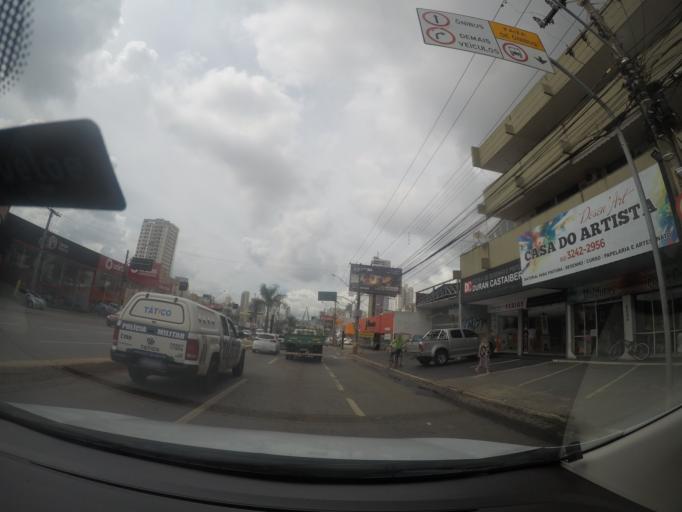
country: BR
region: Goias
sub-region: Goiania
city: Goiania
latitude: -16.7057
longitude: -49.2641
